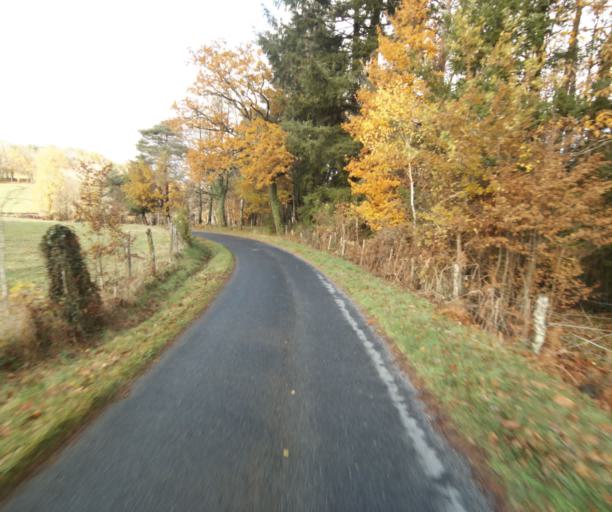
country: FR
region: Limousin
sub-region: Departement de la Correze
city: Chameyrat
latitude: 45.2269
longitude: 1.6886
